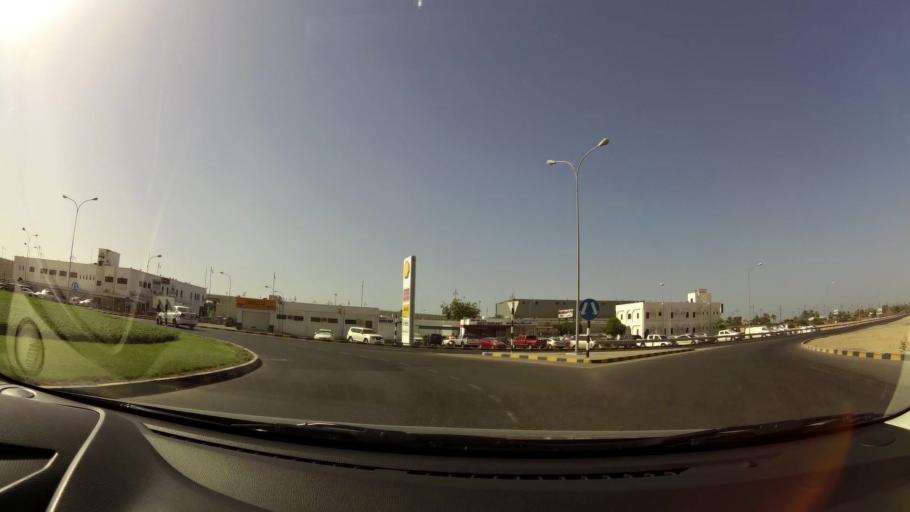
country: OM
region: Muhafazat Masqat
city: Bawshar
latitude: 23.5846
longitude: 58.2975
